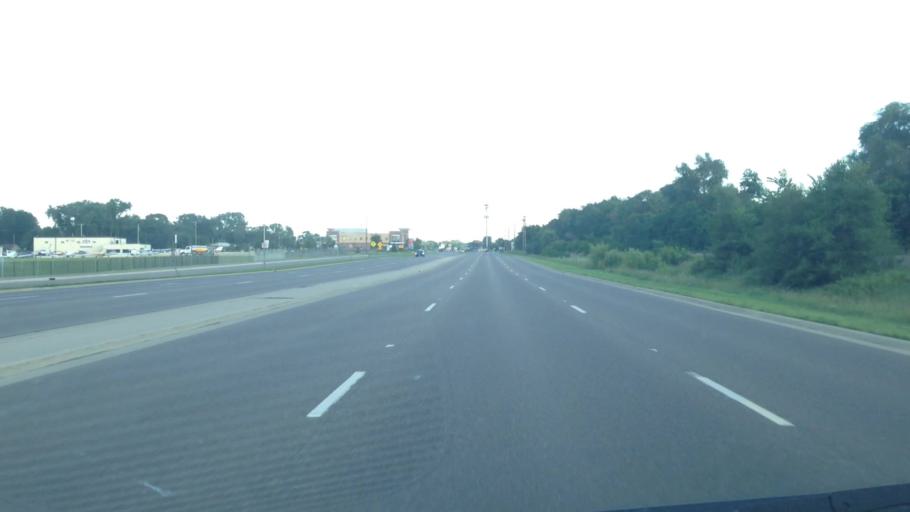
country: US
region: Minnesota
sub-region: Hennepin County
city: Crystal
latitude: 45.0606
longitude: -93.3624
